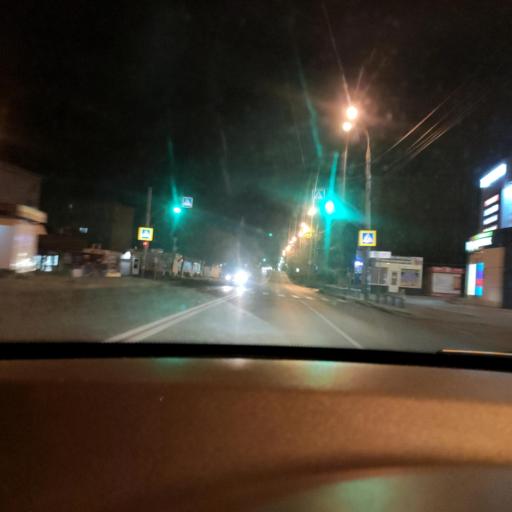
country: RU
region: Samara
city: Samara
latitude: 53.2512
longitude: 50.2382
